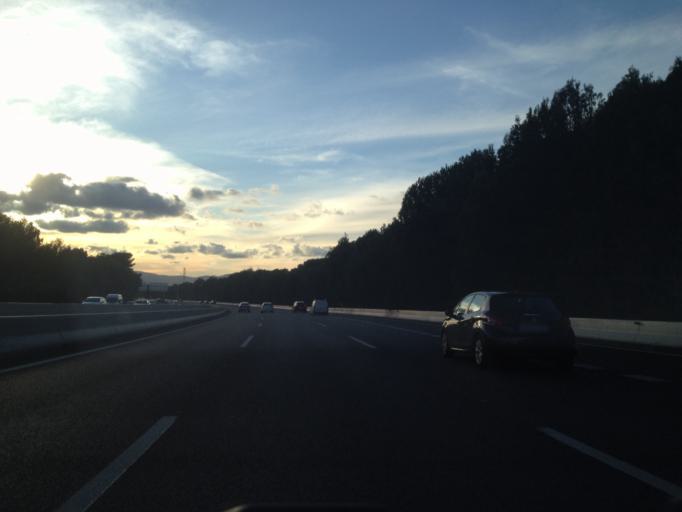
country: ES
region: Balearic Islands
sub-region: Illes Balears
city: Marratxi
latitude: 39.6298
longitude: 2.7228
